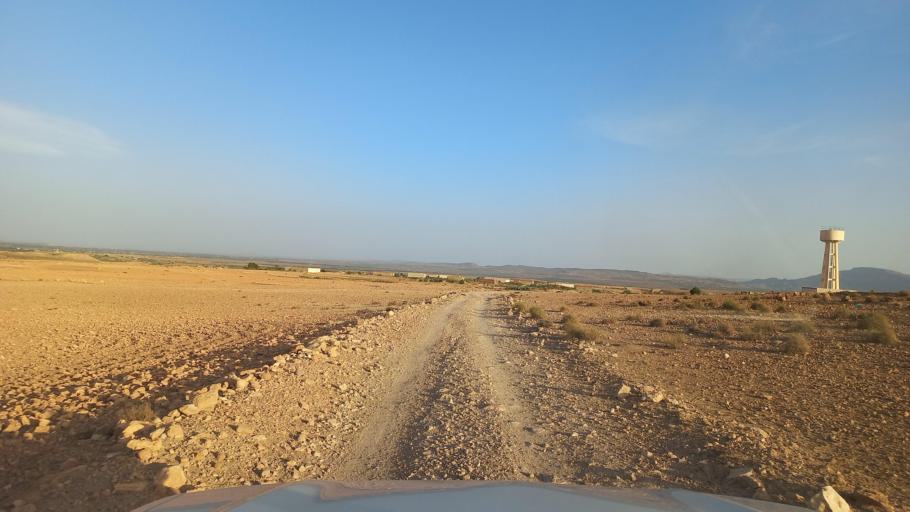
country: TN
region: Al Qasrayn
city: Kasserine
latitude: 35.2802
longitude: 8.9081
